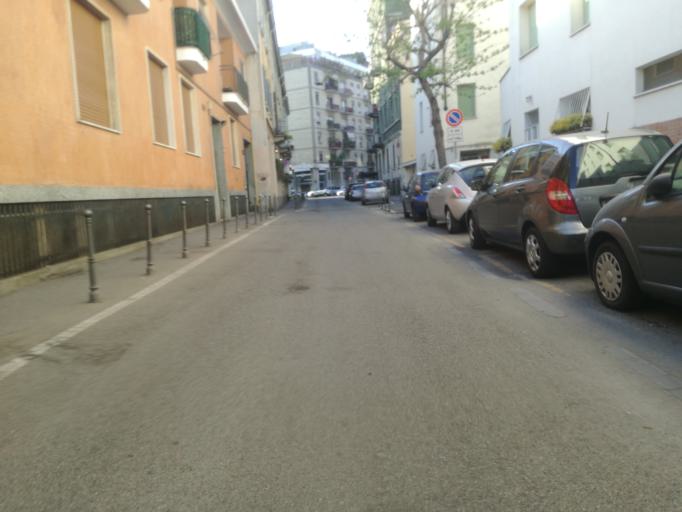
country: IT
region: Lombardy
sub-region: Citta metropolitana di Milano
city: Milano
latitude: 45.4501
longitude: 9.1997
